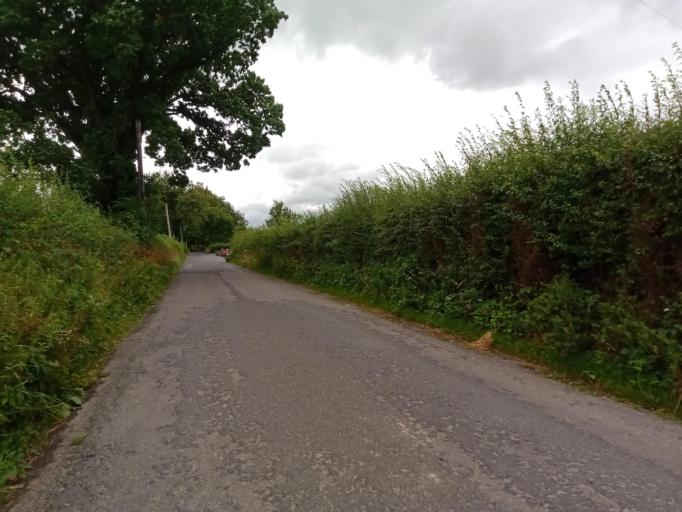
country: IE
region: Leinster
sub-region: Kilkenny
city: Callan
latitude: 52.5738
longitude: -7.3777
